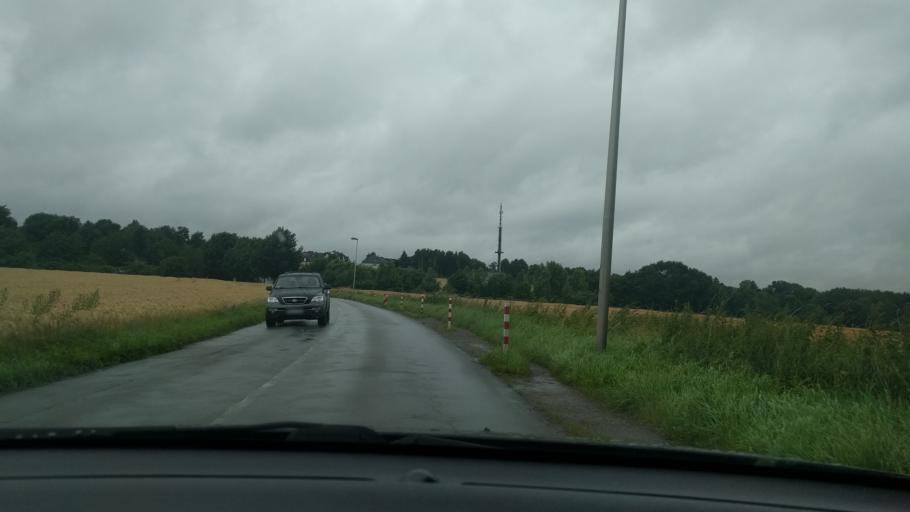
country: DE
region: North Rhine-Westphalia
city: Witten
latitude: 51.4627
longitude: 7.3712
